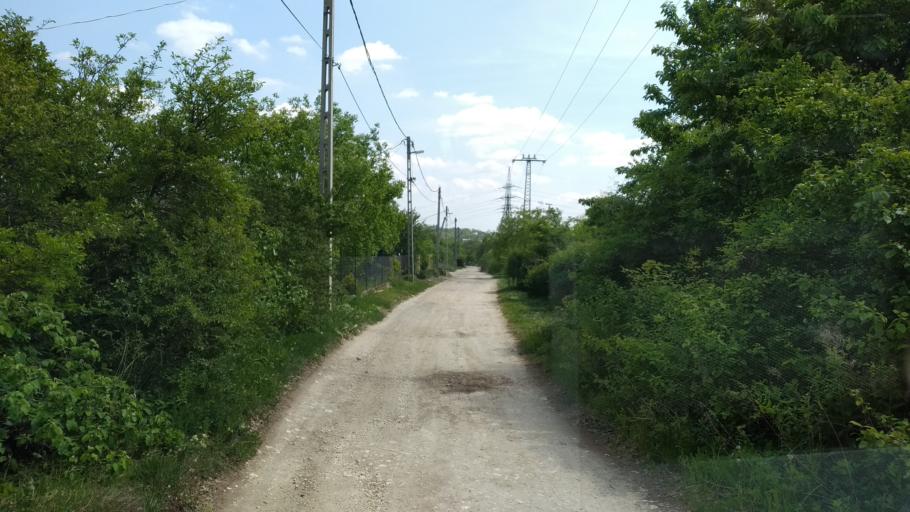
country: HU
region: Pest
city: Urom
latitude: 47.6180
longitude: 19.0253
